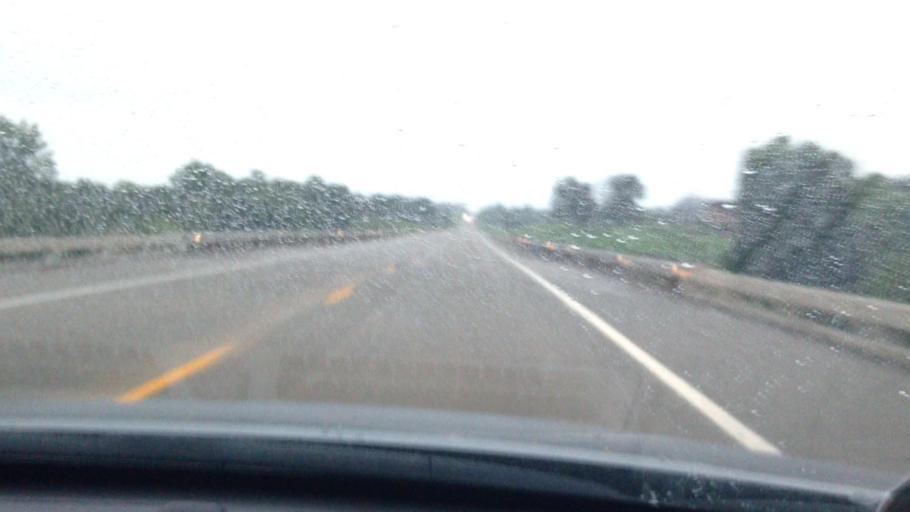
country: US
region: Kansas
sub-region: Brown County
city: Hiawatha
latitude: 39.8324
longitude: -95.5270
